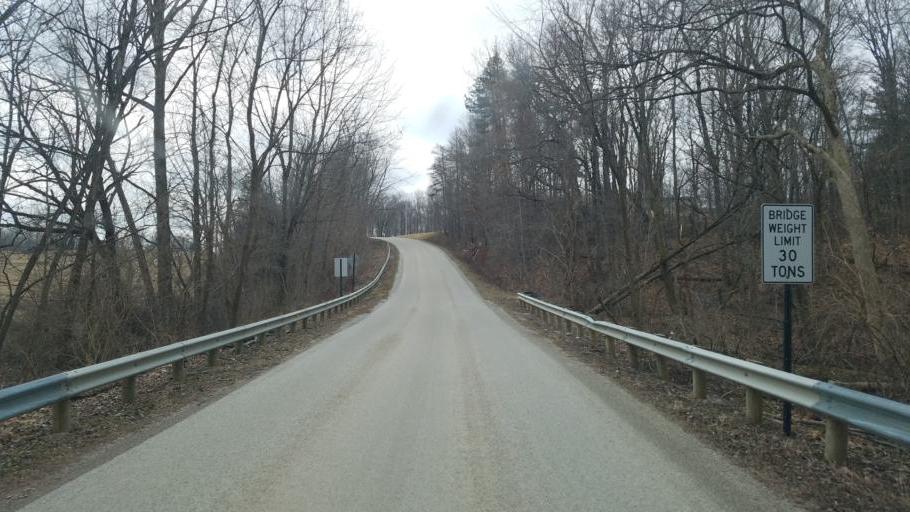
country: US
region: Ohio
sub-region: Morrow County
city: Mount Gilead
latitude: 40.6166
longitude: -82.7867
